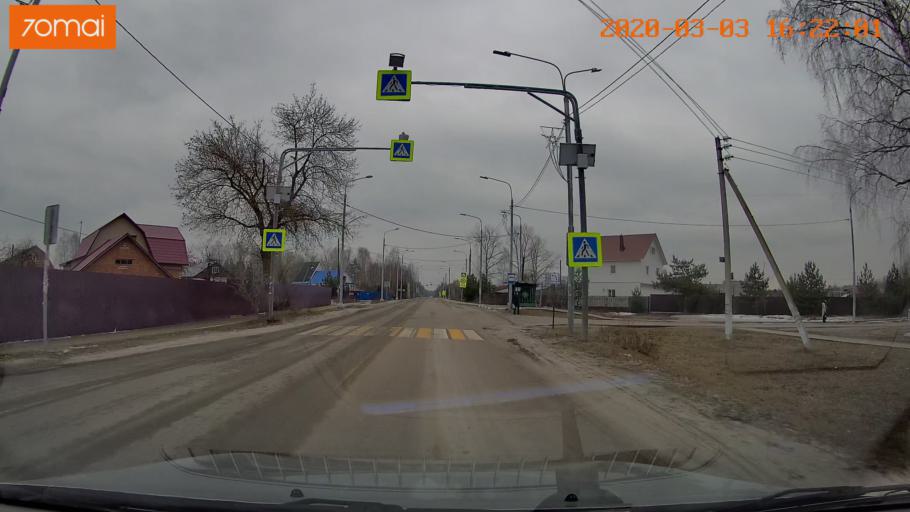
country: RU
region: Moskovskaya
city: Imeni Tsyurupy
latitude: 55.4939
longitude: 38.6467
